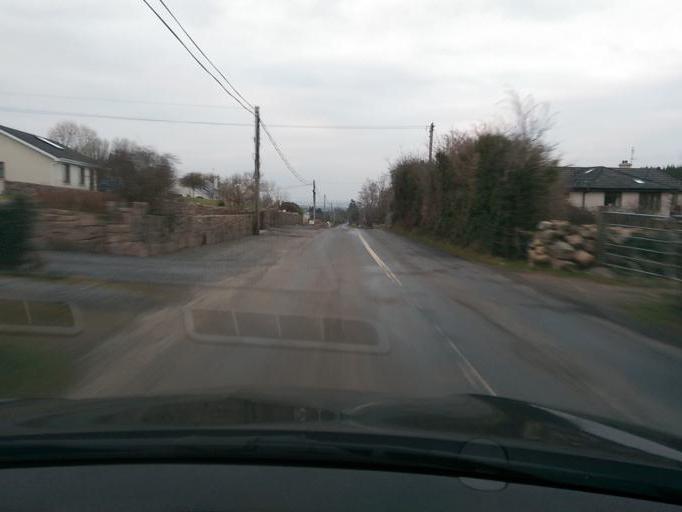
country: IE
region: Connaught
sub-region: County Galway
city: Moycullen
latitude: 53.3006
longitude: -9.1582
